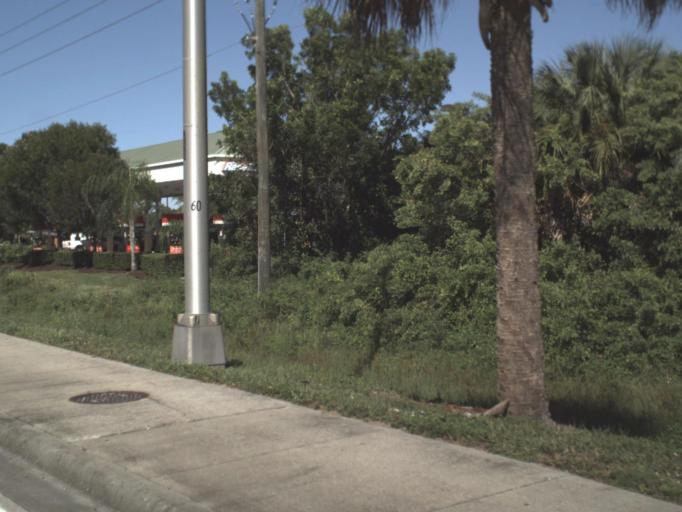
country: US
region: Florida
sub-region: Collier County
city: Vineyards
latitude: 26.2117
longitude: -81.7422
